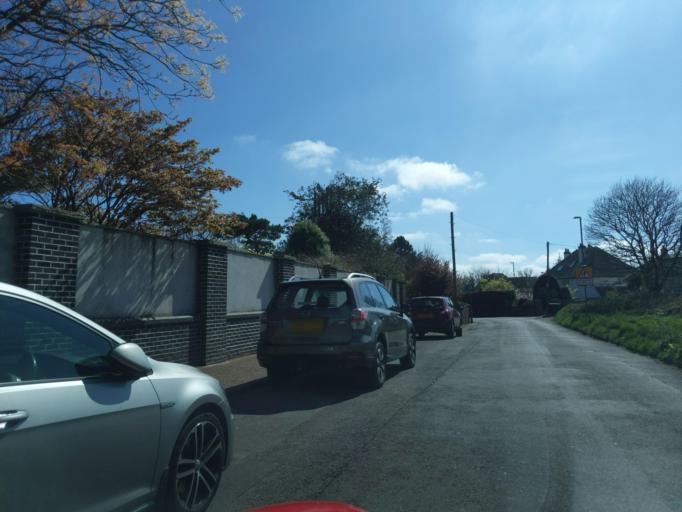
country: GB
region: England
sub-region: Borough of Torbay
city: Paignton
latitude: 50.4005
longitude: -3.5666
